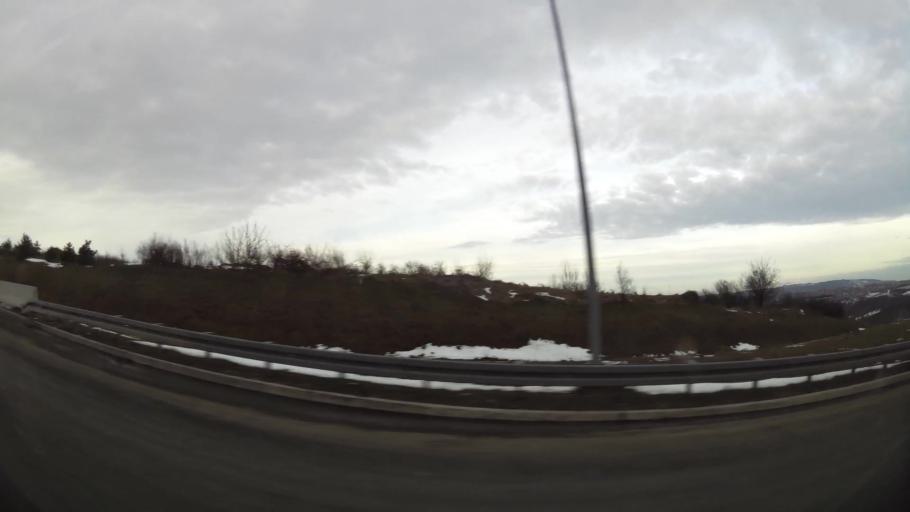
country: RS
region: Central Serbia
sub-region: Belgrade
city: Rakovica
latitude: 44.7132
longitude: 20.4189
